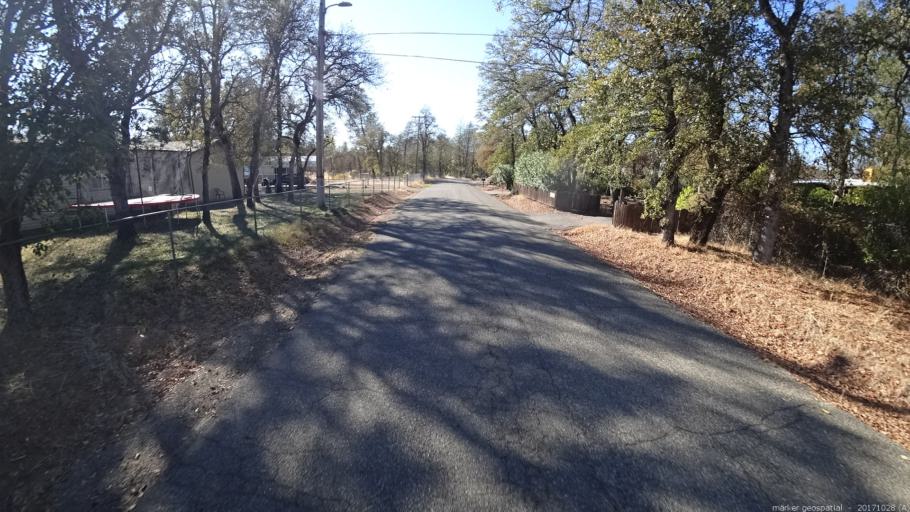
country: US
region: California
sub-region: Shasta County
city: Central Valley (historical)
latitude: 40.6368
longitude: -122.3733
